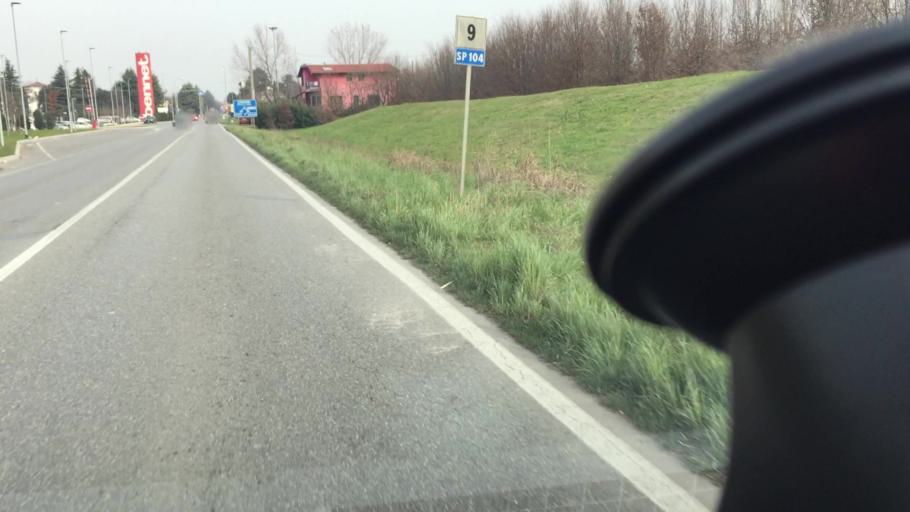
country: IT
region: Lombardy
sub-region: Citta metropolitana di Milano
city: Vaprio d'Adda
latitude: 45.5706
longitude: 9.5199
